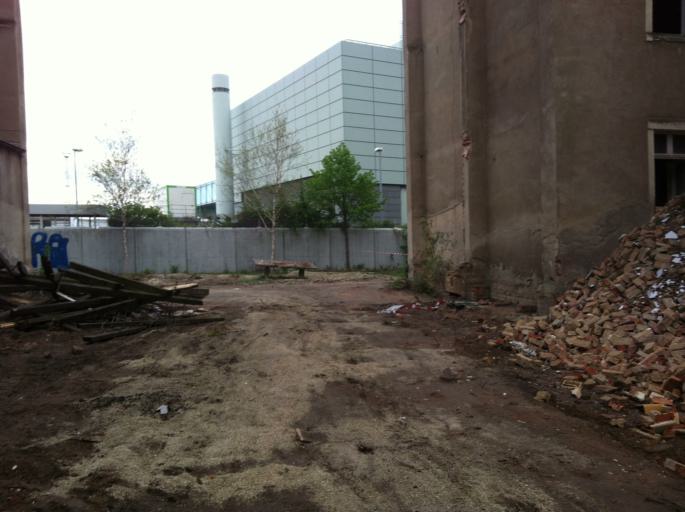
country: DE
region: Saxony
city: Dresden
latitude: 51.0430
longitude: 13.7084
